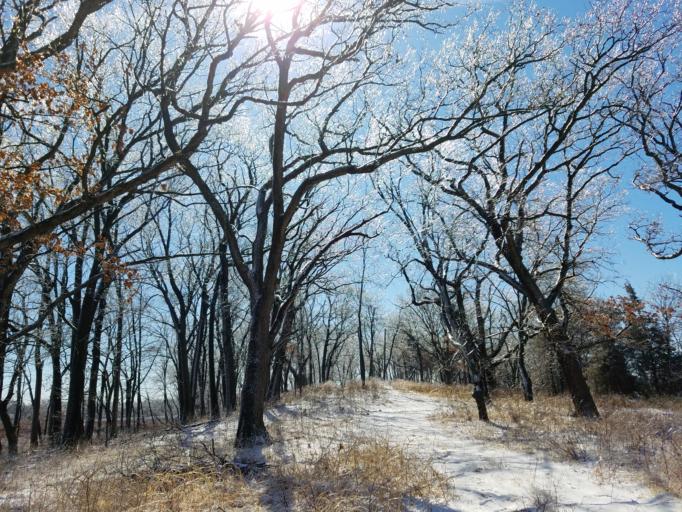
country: US
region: Wisconsin
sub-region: Jefferson County
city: Lake Ripley
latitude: 42.9824
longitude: -88.9806
